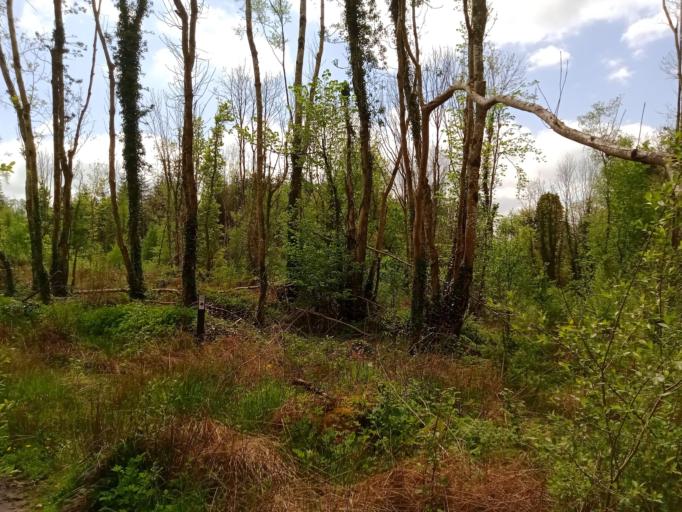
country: IE
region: Leinster
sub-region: Kilkenny
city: Castlecomer
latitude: 52.8167
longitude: -7.2032
